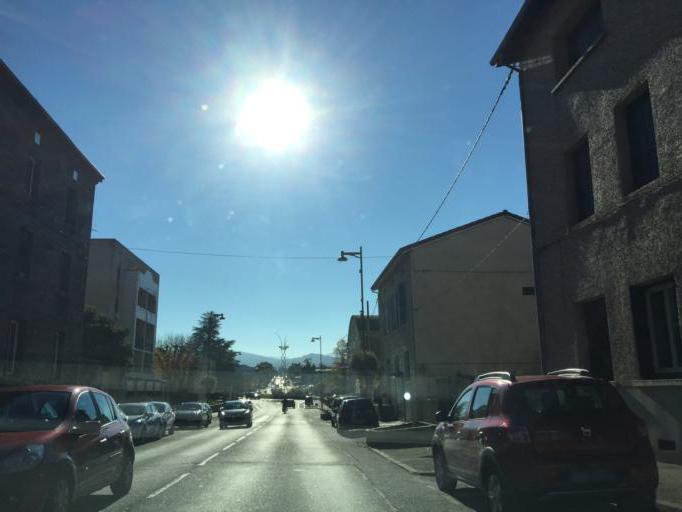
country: FR
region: Rhone-Alpes
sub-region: Departement de la Loire
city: Lorette
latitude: 45.5050
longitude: 4.5700
